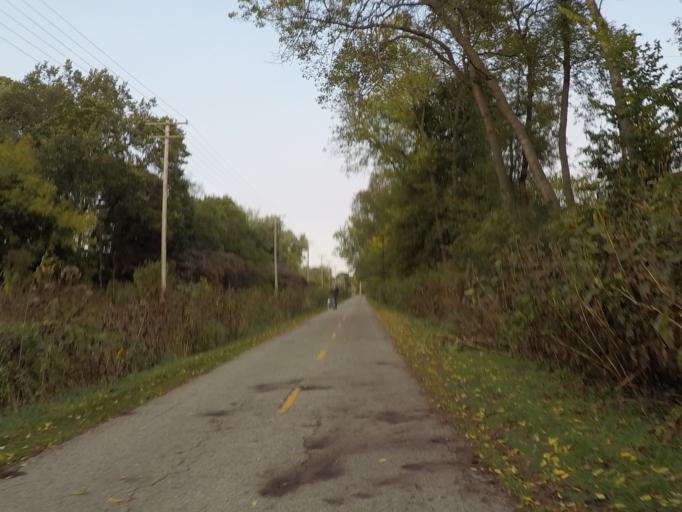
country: US
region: Wisconsin
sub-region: Dane County
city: Shorewood Hills
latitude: 43.0452
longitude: -89.4539
